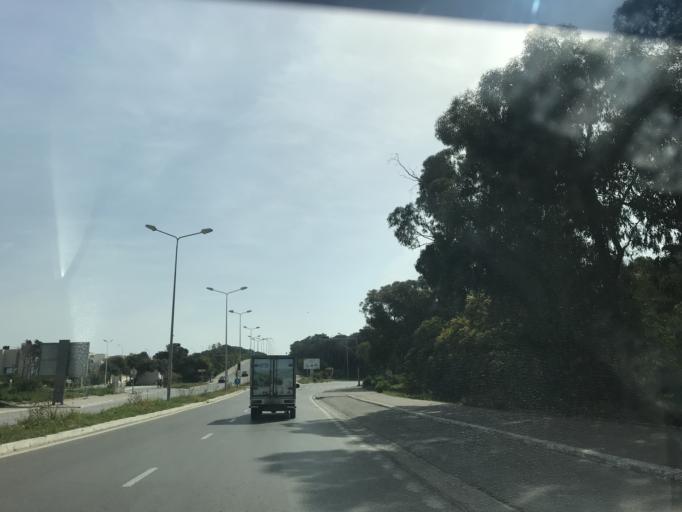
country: TN
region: Tunis
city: Al Marsa
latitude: 36.9201
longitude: 10.2896
